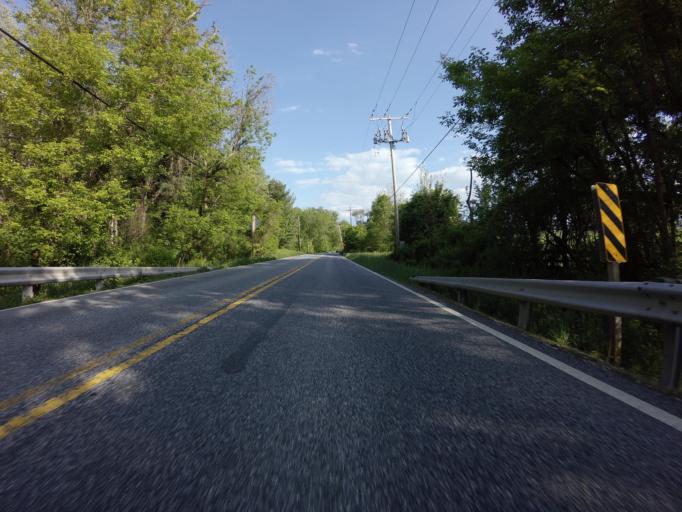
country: US
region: Maryland
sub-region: Baltimore County
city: Hunt Valley
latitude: 39.5192
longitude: -76.7192
